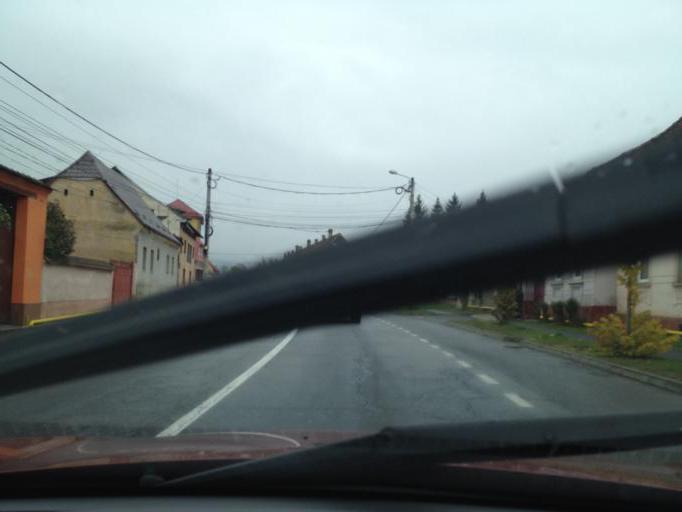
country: RO
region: Brasov
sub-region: Comuna Cristian
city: Cristian
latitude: 45.6183
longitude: 25.4764
